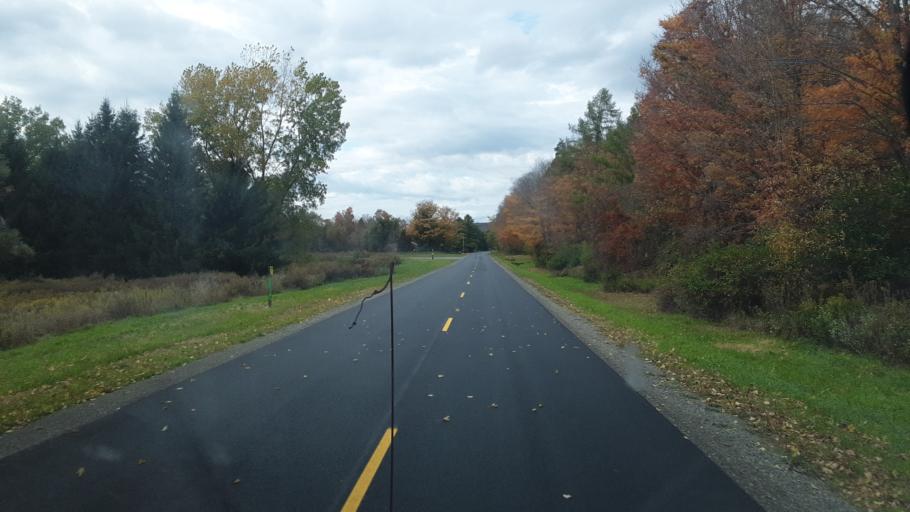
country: US
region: New York
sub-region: Allegany County
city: Alfred
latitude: 42.3665
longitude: -77.7761
